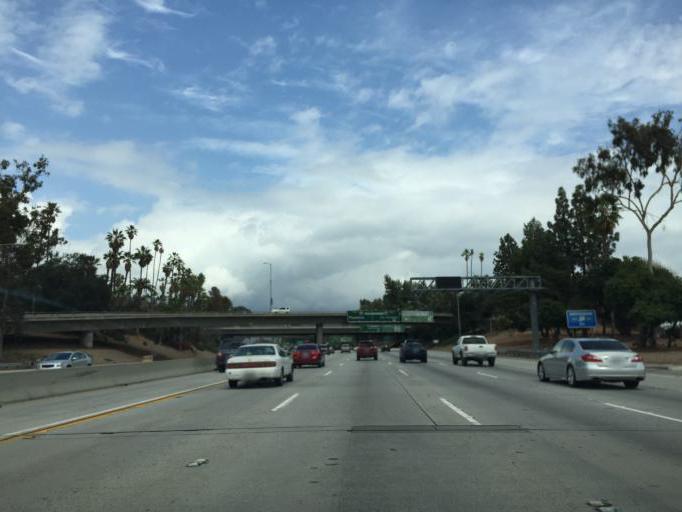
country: US
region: California
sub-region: Los Angeles County
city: Pasadena
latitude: 34.1460
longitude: -118.1639
